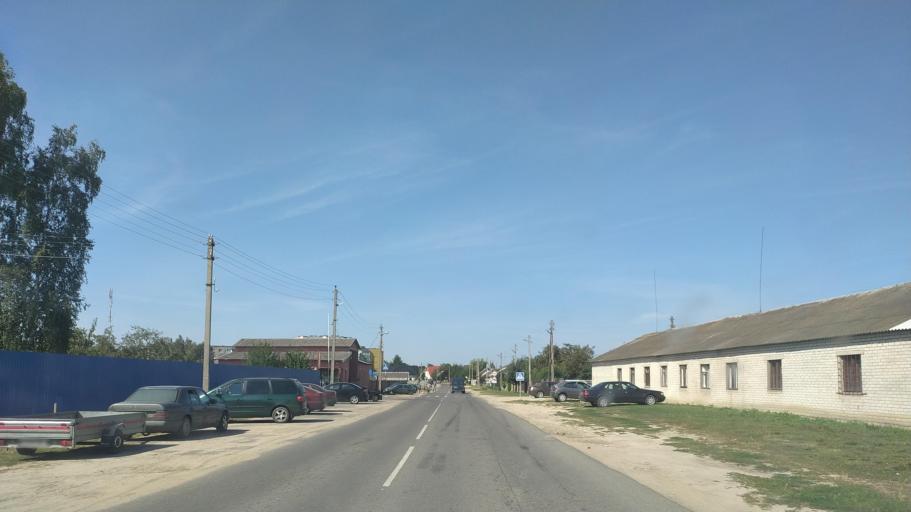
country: BY
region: Brest
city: Byaroza
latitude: 52.5257
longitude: 24.9890
